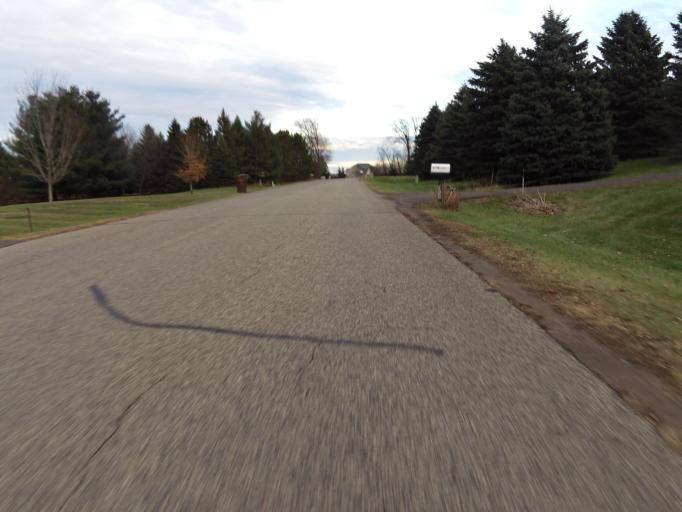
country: US
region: Minnesota
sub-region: Washington County
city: Oak Park Heights
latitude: 45.0122
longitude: -92.8037
